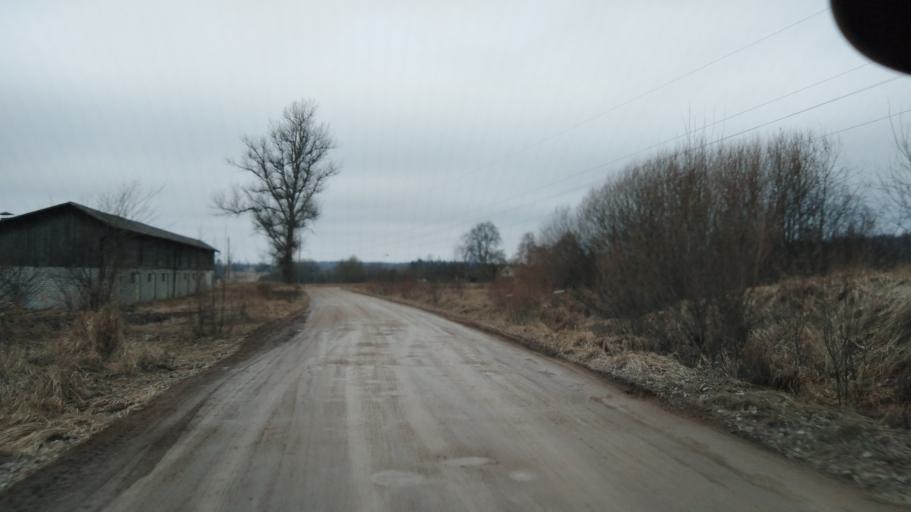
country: LV
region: Kuldigas Rajons
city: Kuldiga
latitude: 56.9831
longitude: 21.9733
